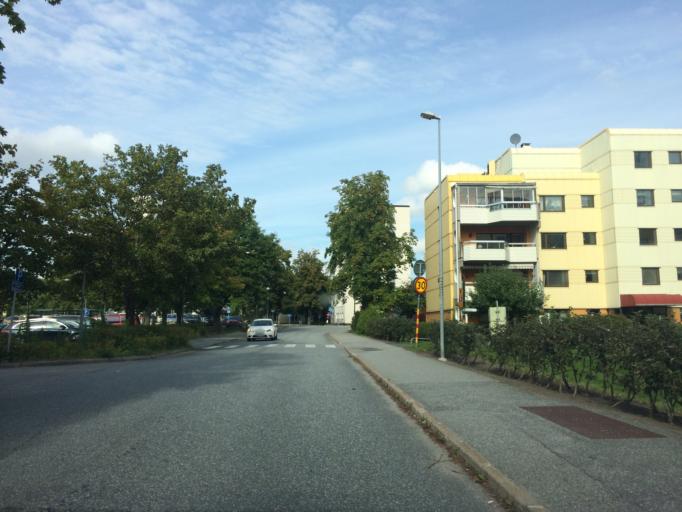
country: SE
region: Stockholm
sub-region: Sollentuna Kommun
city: Sollentuna
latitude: 59.4441
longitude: 17.9345
